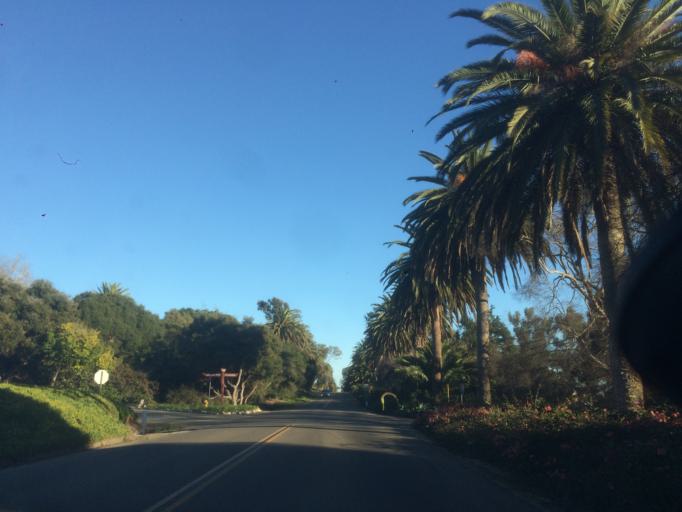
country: US
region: California
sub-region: Santa Barbara County
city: Mission Canyon
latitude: 34.4117
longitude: -119.7645
